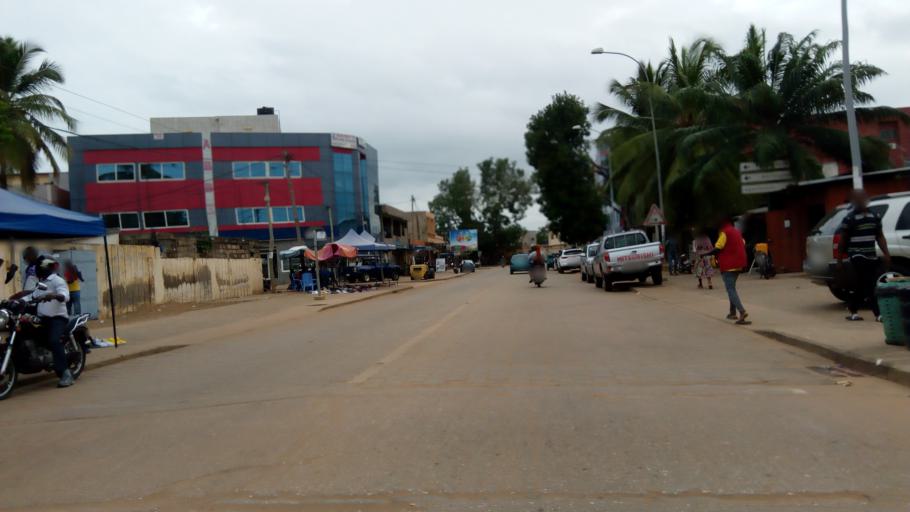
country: TG
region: Maritime
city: Lome
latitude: 6.1825
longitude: 1.1958
